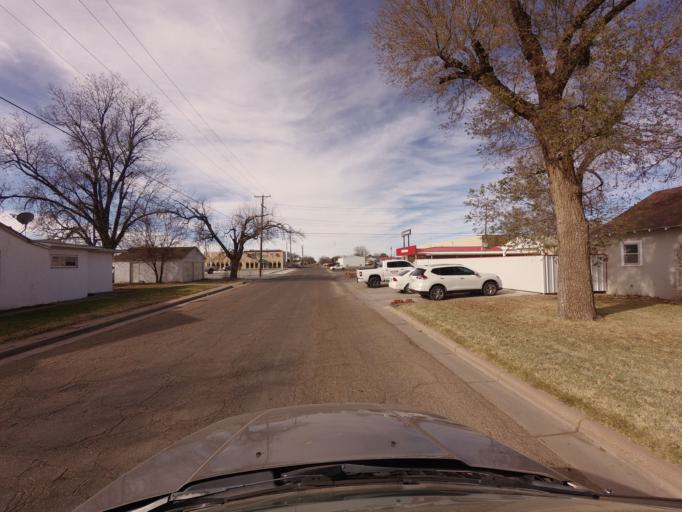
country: US
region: New Mexico
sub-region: Curry County
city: Clovis
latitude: 34.4089
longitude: -103.2043
